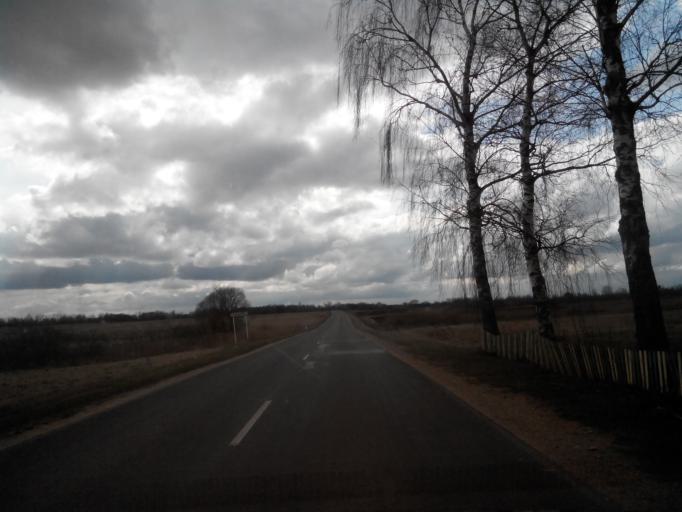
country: BY
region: Vitebsk
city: Pastavy
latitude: 55.1407
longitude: 26.9526
